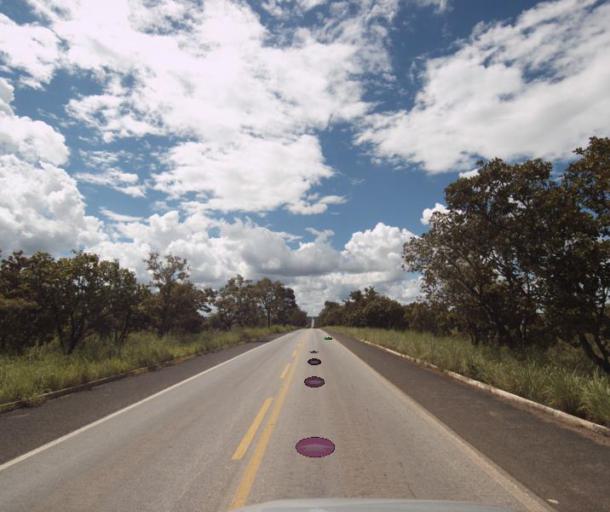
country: BR
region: Goias
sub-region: Porangatu
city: Porangatu
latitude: -13.8591
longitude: -49.0499
